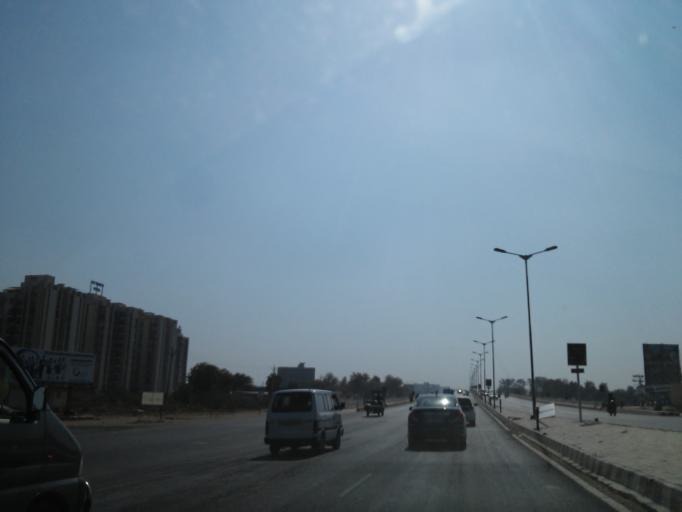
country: IN
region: Gujarat
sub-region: Gandhinagar
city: Adalaj
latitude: 23.1059
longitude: 72.5339
